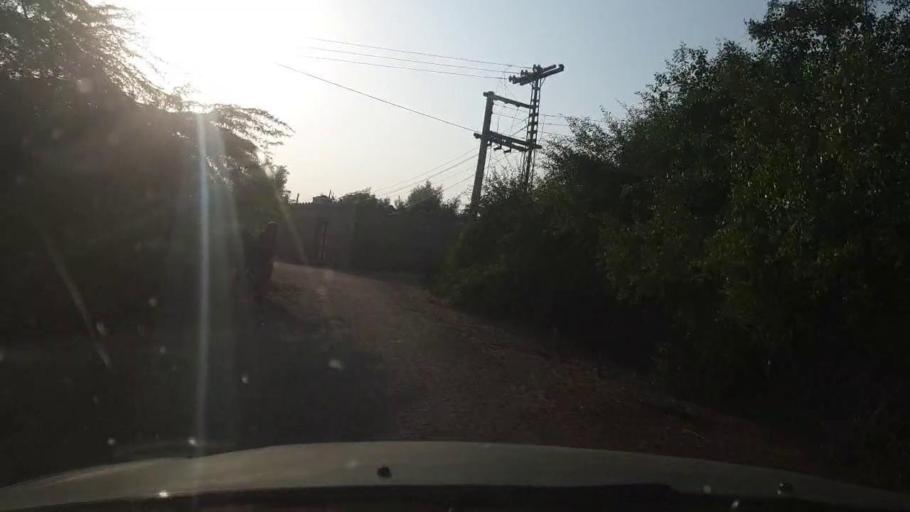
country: PK
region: Sindh
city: Tando Ghulam Ali
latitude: 25.1525
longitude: 68.9602
